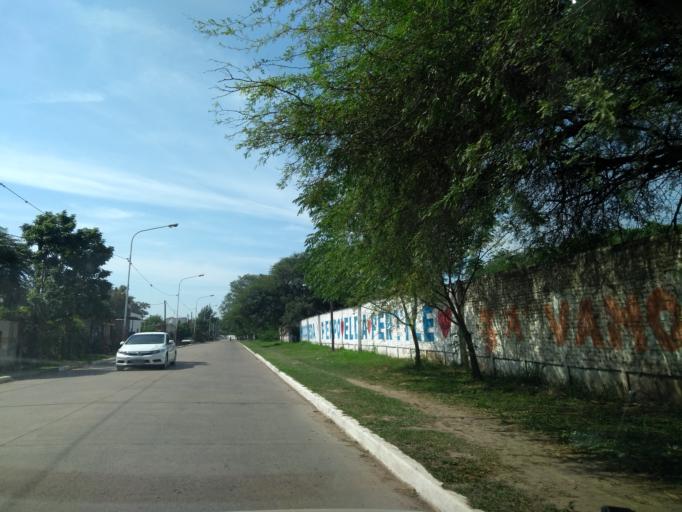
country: AR
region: Chaco
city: Barranqueras
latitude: -27.4645
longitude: -58.9564
